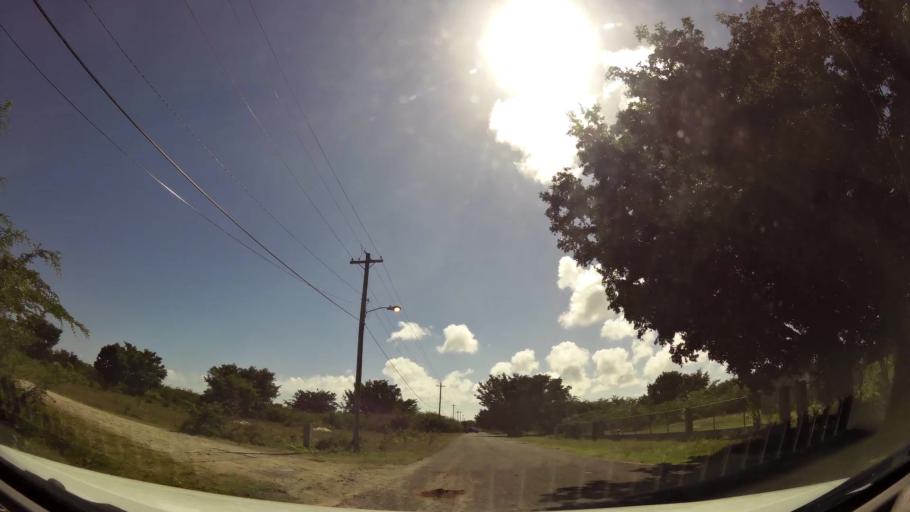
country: AG
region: Barbuda
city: Codrington
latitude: 17.6243
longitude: -61.8280
